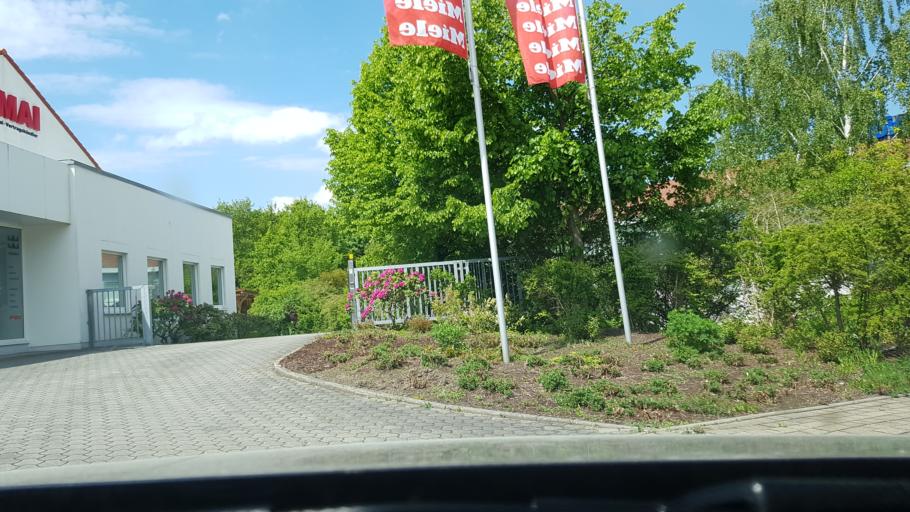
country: DE
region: Saxony
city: Wilsdruff
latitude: 51.0363
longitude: 13.5819
